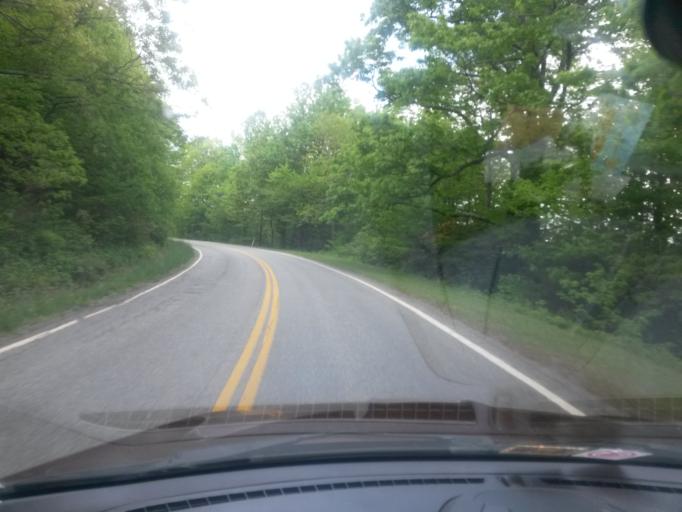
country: US
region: Virginia
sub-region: Floyd County
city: Floyd
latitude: 36.7695
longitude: -80.3857
